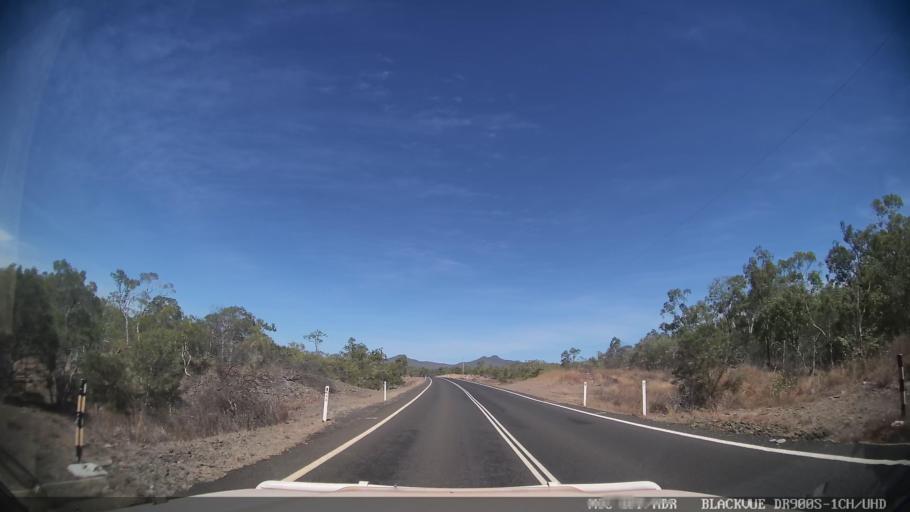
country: AU
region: Queensland
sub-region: Cook
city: Cooktown
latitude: -15.7079
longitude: 144.6110
